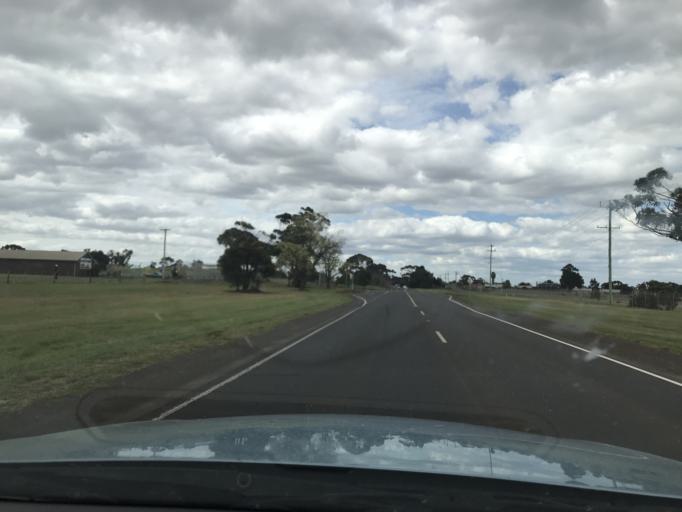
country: AU
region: Victoria
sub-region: Hobsons Bay
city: Laverton
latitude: -37.8531
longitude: 144.7651
